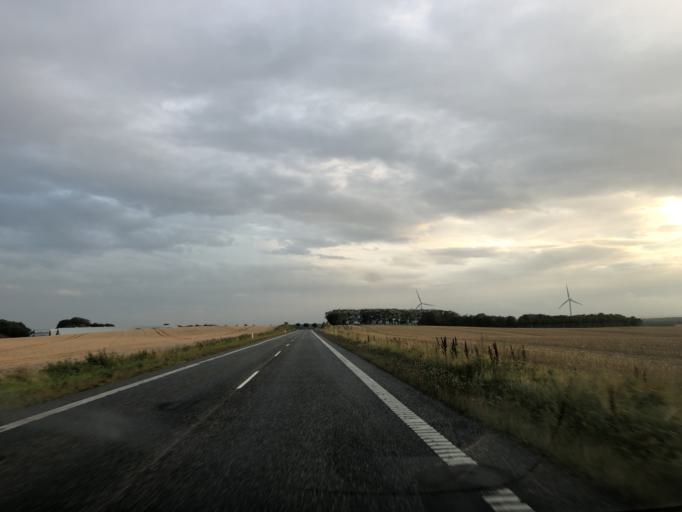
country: DK
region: Central Jutland
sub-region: Holstebro Kommune
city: Vinderup
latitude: 56.5836
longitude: 8.8794
